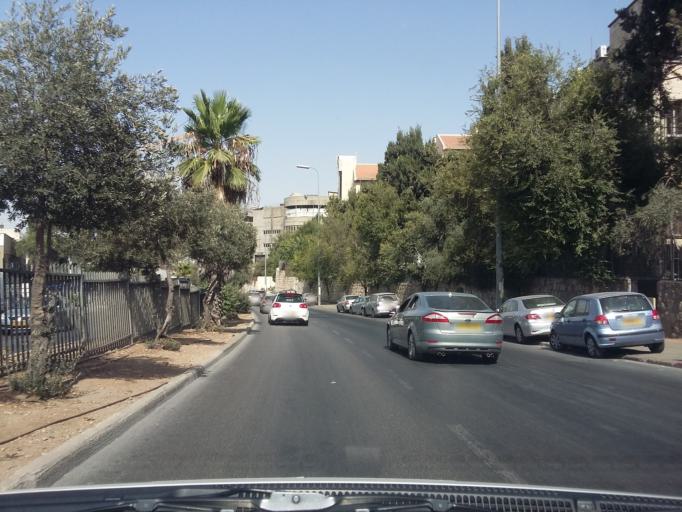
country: IL
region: Jerusalem
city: West Jerusalem
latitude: 31.7921
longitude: 35.2114
